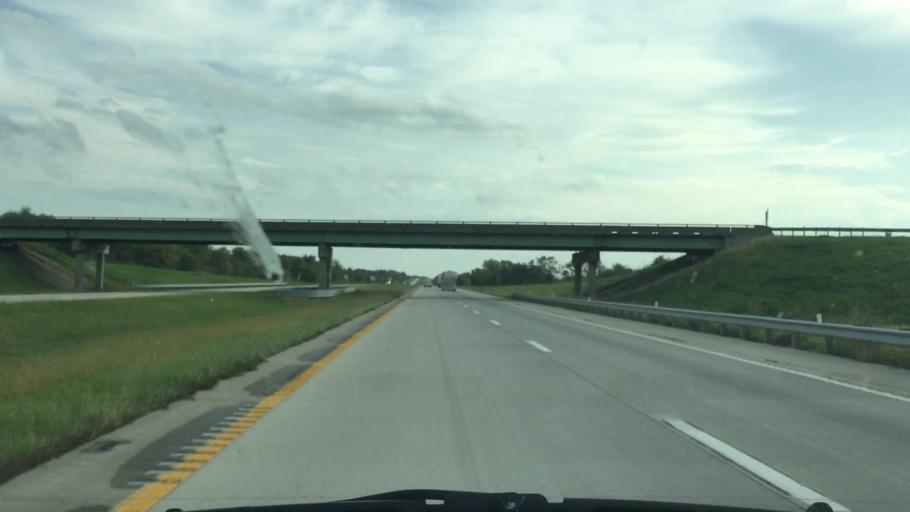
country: US
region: Missouri
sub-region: Daviess County
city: Gallatin
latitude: 39.9969
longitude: -94.0959
